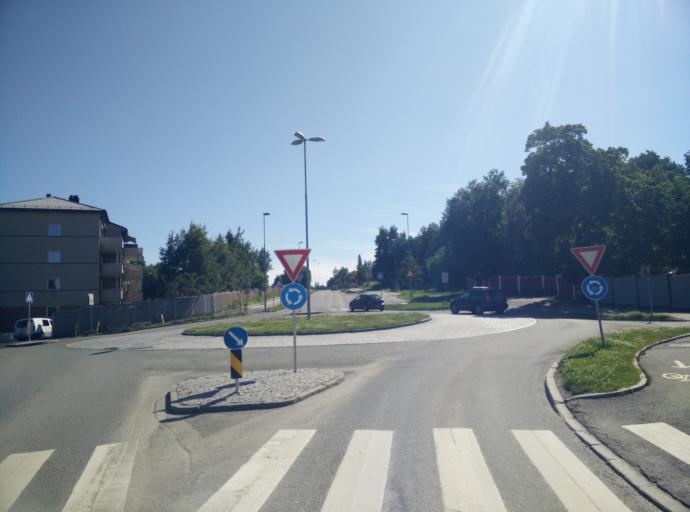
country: NO
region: Sor-Trondelag
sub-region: Trondheim
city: Trondheim
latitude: 63.4040
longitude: 10.3584
